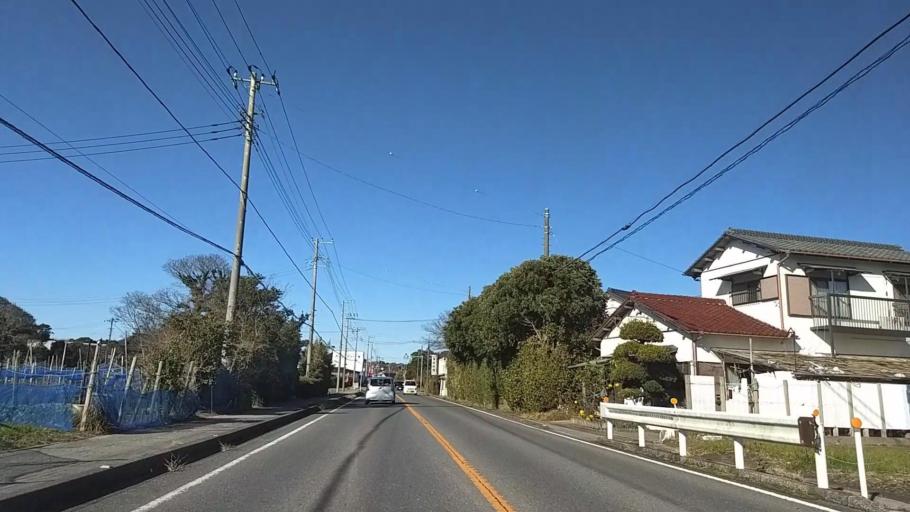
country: JP
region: Chiba
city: Ohara
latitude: 35.3192
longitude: 140.4033
